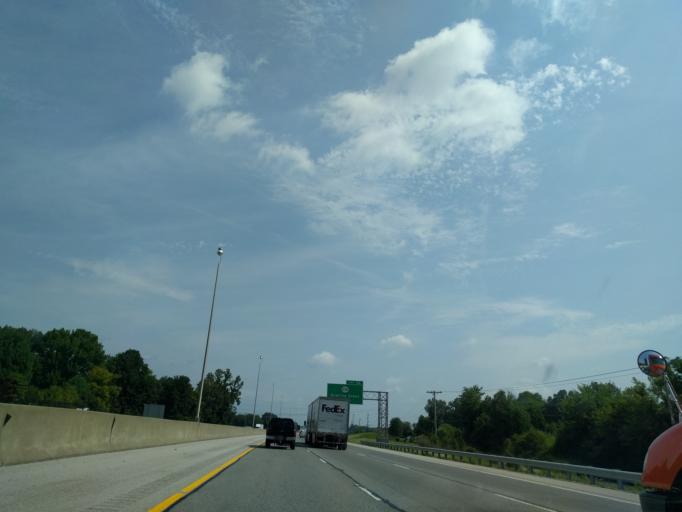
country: US
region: Kentucky
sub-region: Warren County
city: Bowling Green
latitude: 36.9474
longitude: -86.4105
